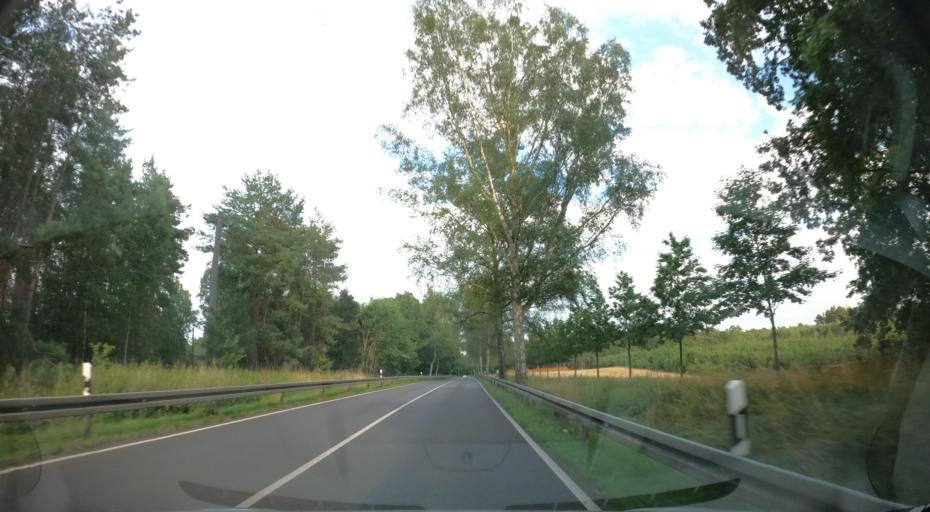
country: PL
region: West Pomeranian Voivodeship
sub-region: Powiat policki
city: Dobra
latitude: 53.4546
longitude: 14.3458
